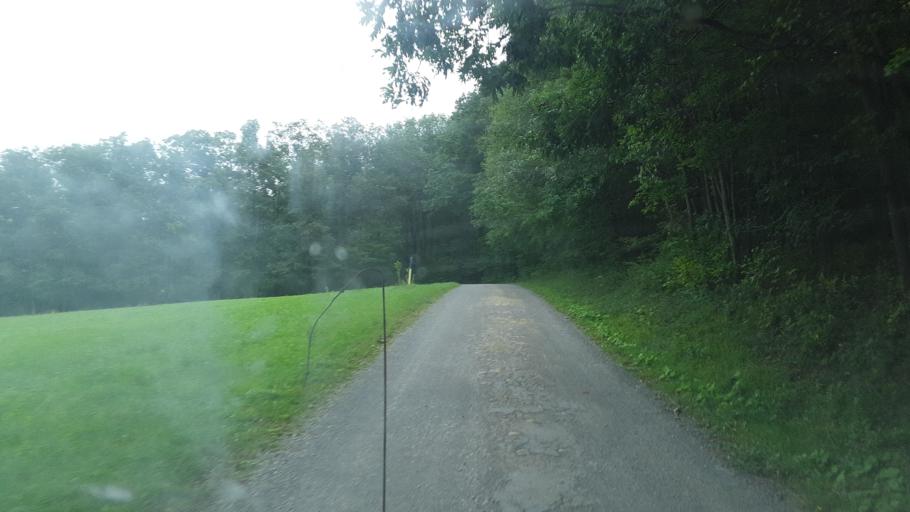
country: US
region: Pennsylvania
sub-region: Jefferson County
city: Punxsutawney
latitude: 40.9672
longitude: -79.1277
